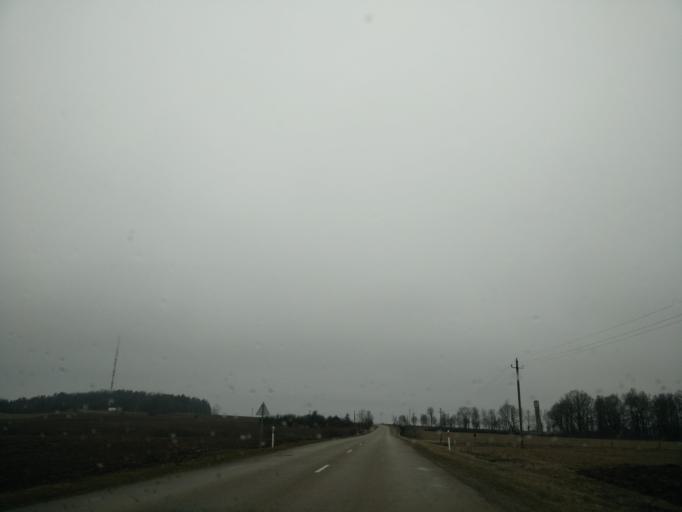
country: LT
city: Ariogala
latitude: 55.3440
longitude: 23.3932
